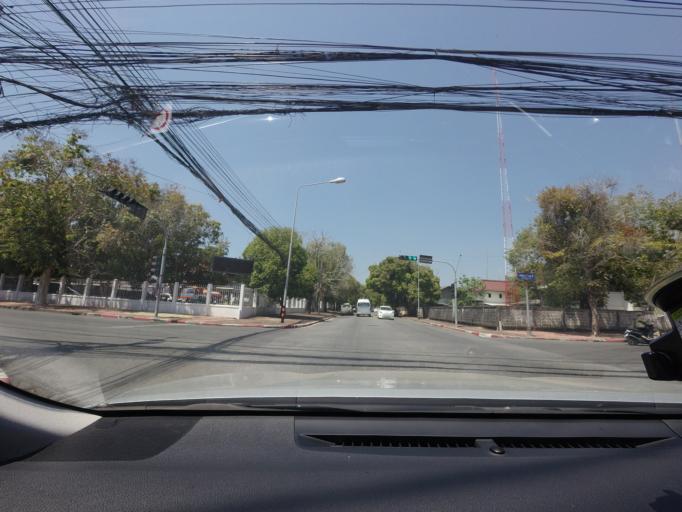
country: TH
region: Yala
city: Yala
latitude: 6.5411
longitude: 101.2827
